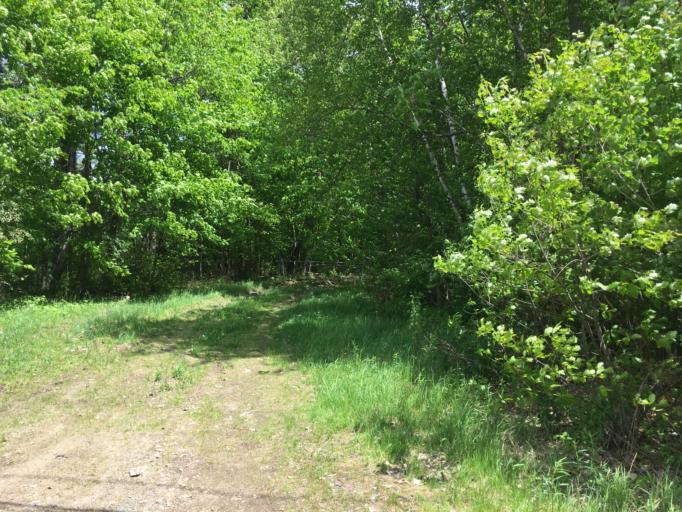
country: US
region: New Hampshire
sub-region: Rockingham County
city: Exeter
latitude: 42.9712
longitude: -70.9593
